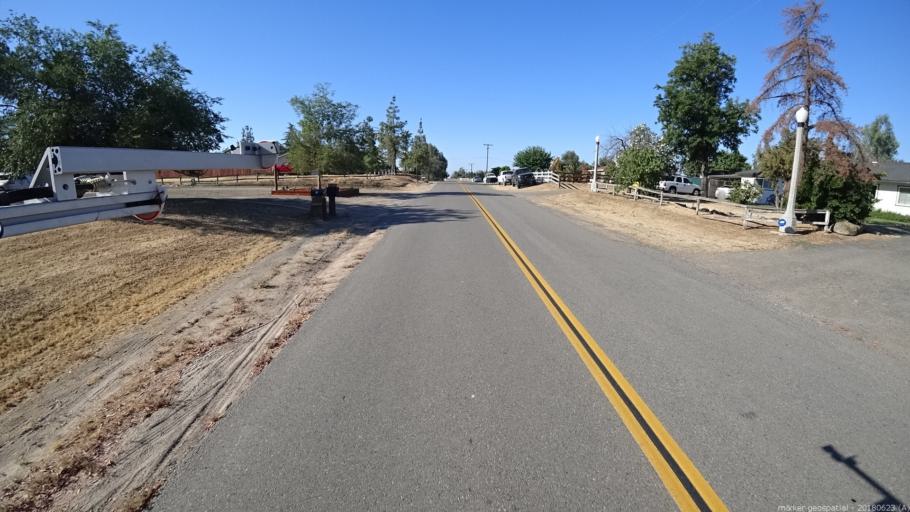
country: US
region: California
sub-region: Madera County
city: Bonadelle Ranchos-Madera Ranchos
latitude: 36.9653
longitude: -119.8014
